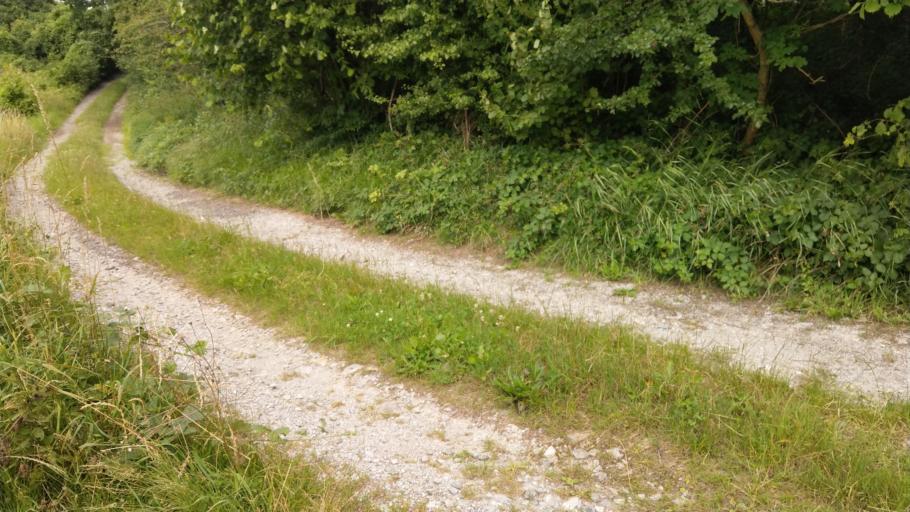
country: BE
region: Wallonia
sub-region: Province de Namur
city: Couvin
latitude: 50.0605
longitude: 4.4319
